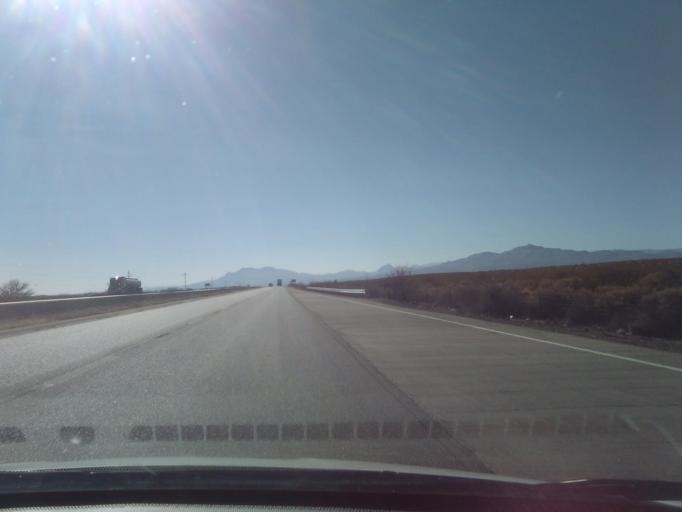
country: US
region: New Mexico
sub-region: Socorro County
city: Socorro
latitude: 34.2846
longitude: -106.8975
